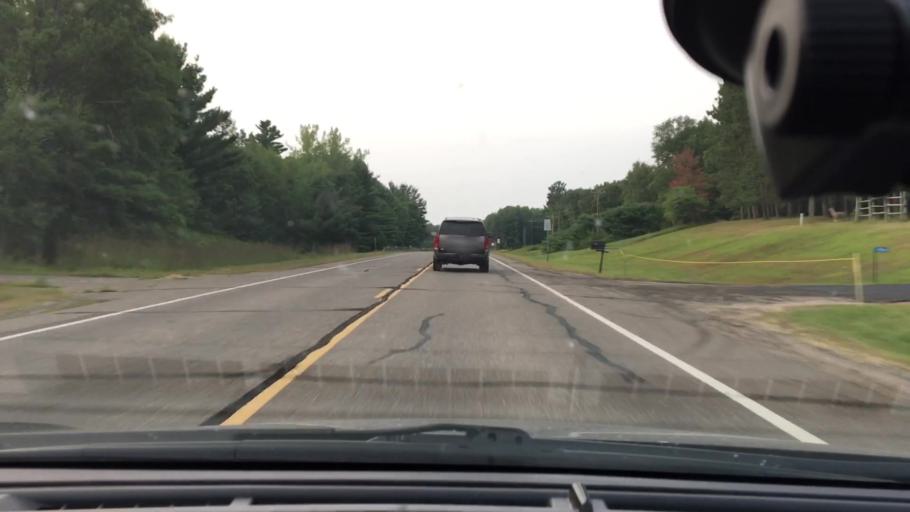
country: US
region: Minnesota
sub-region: Crow Wing County
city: Crosby
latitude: 46.4297
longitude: -93.8734
